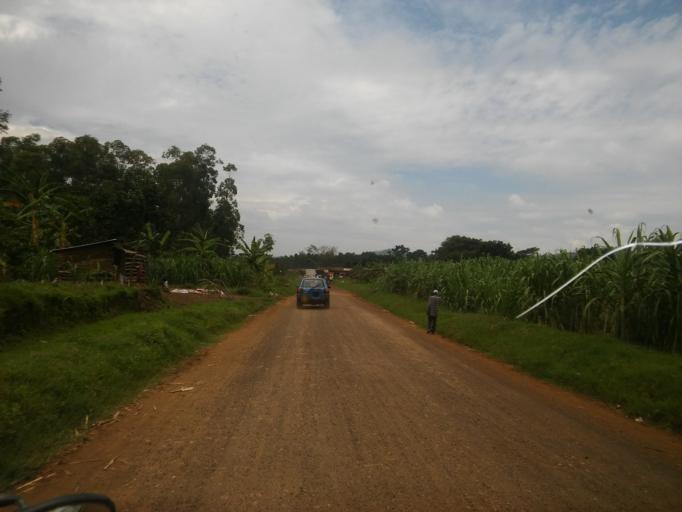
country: UG
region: Eastern Region
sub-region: Bududa District
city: Bududa
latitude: 0.9366
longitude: 34.2835
